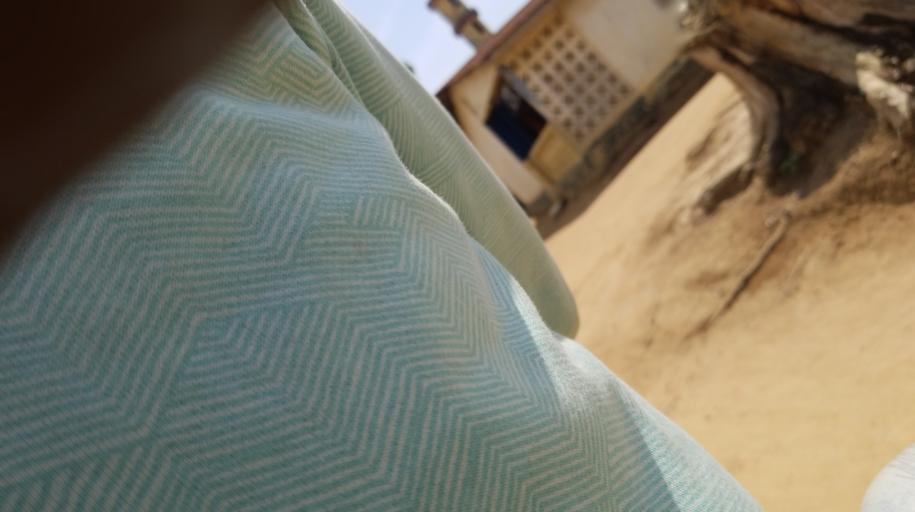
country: SL
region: Western Area
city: Waterloo
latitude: 8.3234
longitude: -13.0536
